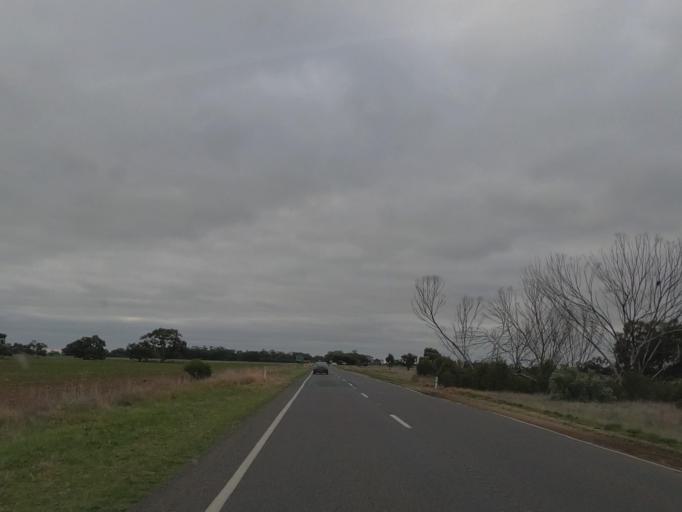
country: AU
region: Victoria
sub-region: Greater Bendigo
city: Long Gully
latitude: -36.2141
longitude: 143.9556
